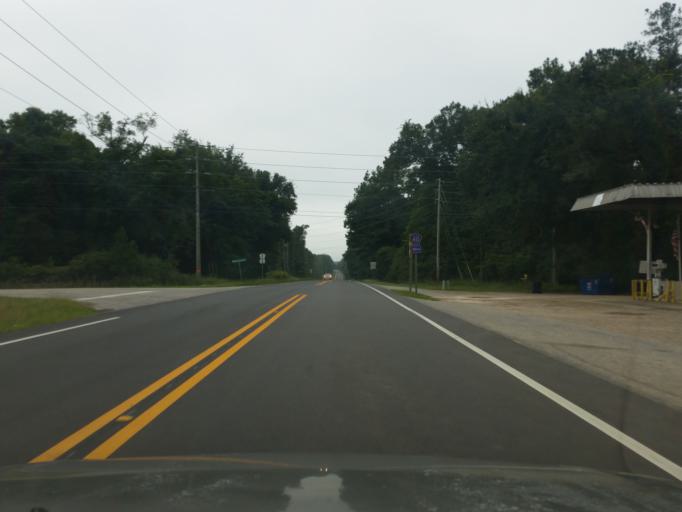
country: US
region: Alabama
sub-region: Baldwin County
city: Spanish Fort
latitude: 30.7816
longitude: -87.8791
